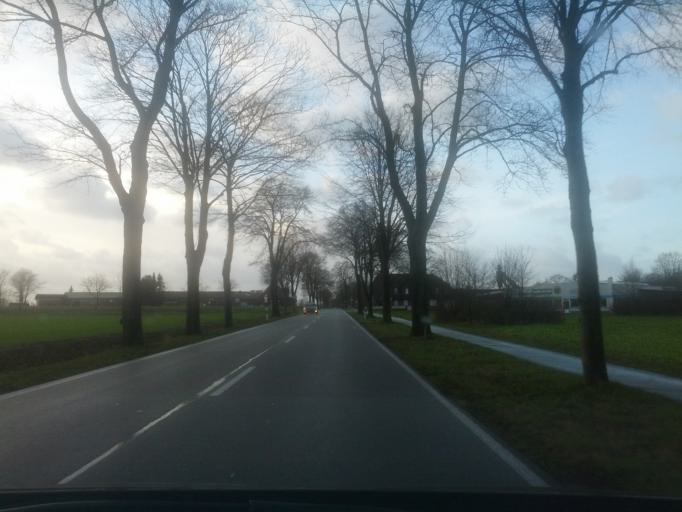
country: DE
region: Lower Saxony
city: Hamersen
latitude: 53.2603
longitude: 9.4885
